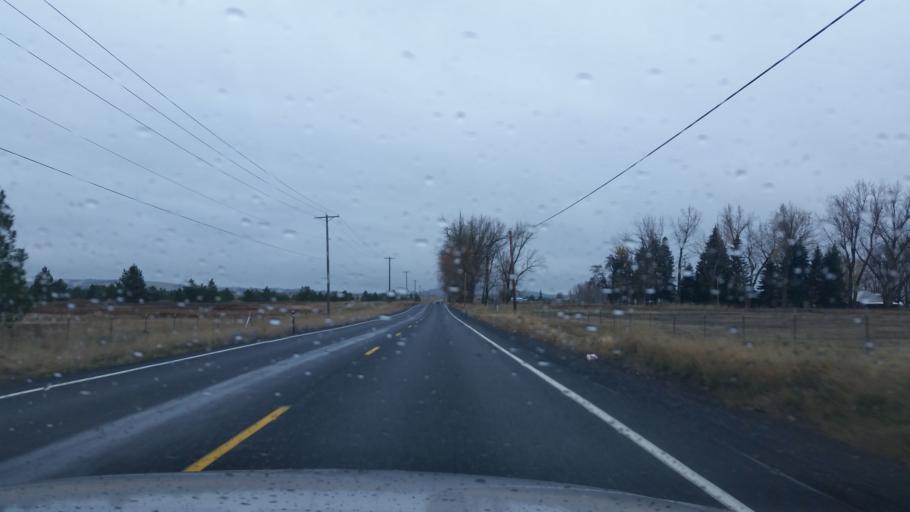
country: US
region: Washington
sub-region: Spokane County
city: Airway Heights
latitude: 47.6228
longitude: -117.6041
